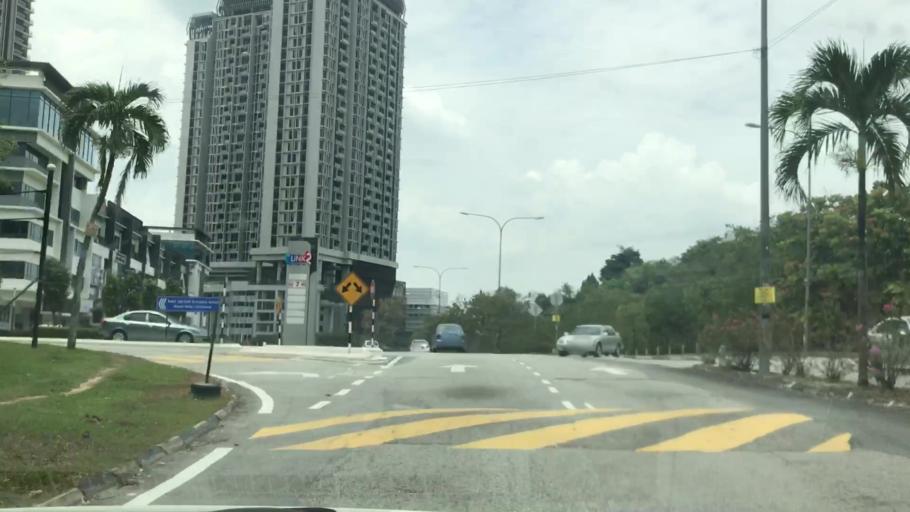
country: MY
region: Selangor
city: Kampong Baharu Balakong
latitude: 3.0526
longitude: 101.6777
